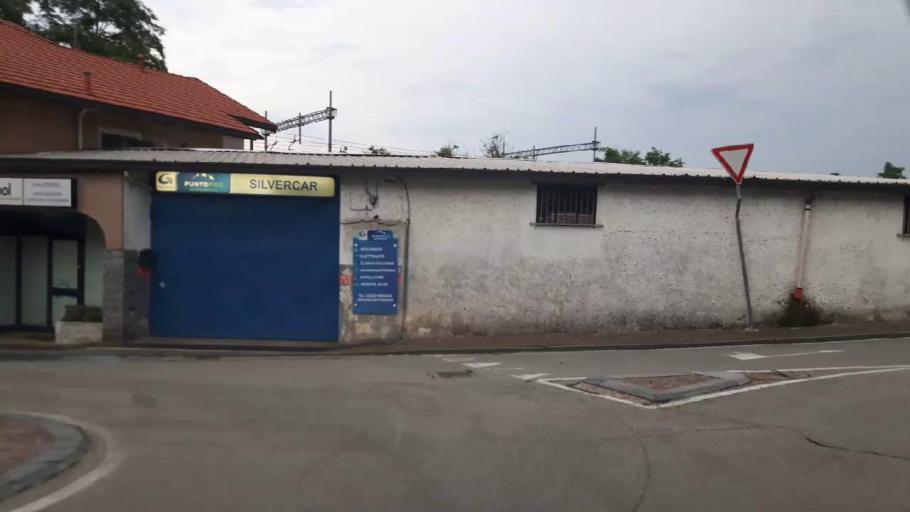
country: IT
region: Piedmont
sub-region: Provincia Verbano-Cusio-Ossola
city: Baveno
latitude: 45.9077
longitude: 8.5016
